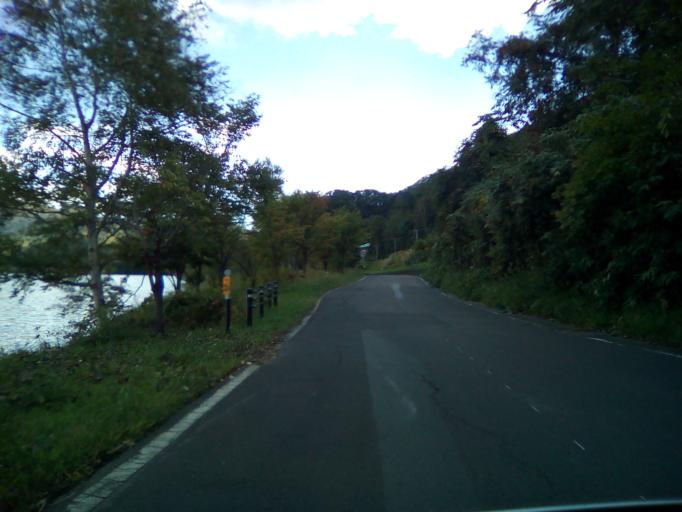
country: JP
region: Hokkaido
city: Date
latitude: 42.5828
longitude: 140.7955
